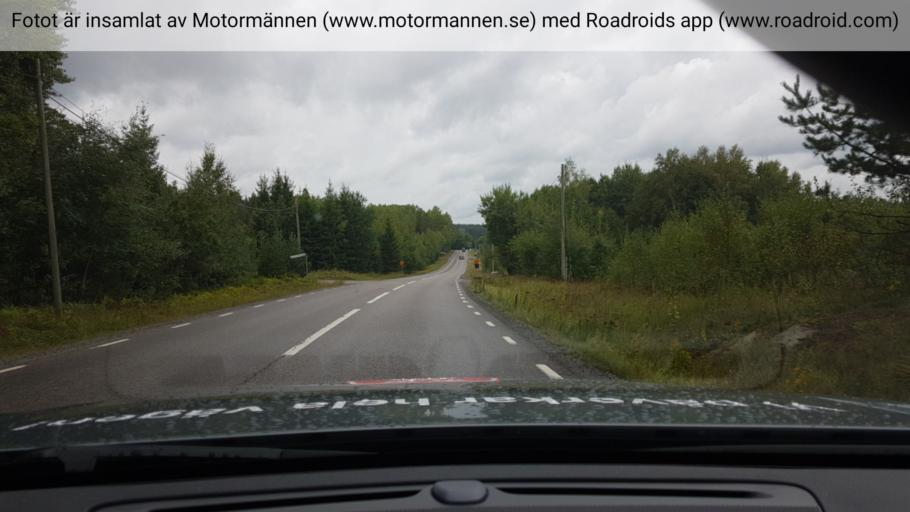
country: SE
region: Stockholm
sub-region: Botkyrka Kommun
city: Tullinge
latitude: 59.1754
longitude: 17.9291
